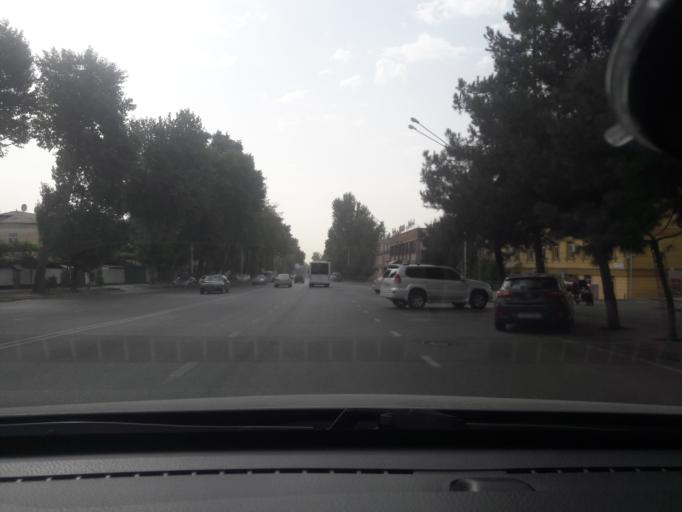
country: TJ
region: Dushanbe
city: Dushanbe
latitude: 38.5778
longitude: 68.8022
